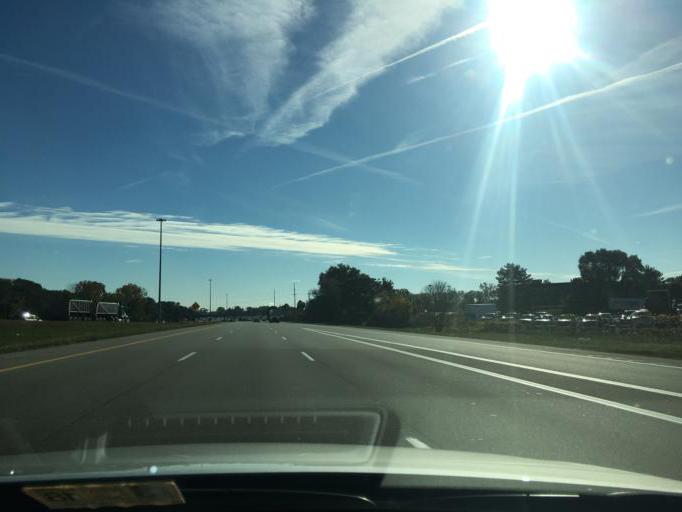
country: US
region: Michigan
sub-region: Wayne County
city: Plymouth
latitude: 42.3846
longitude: -83.4305
